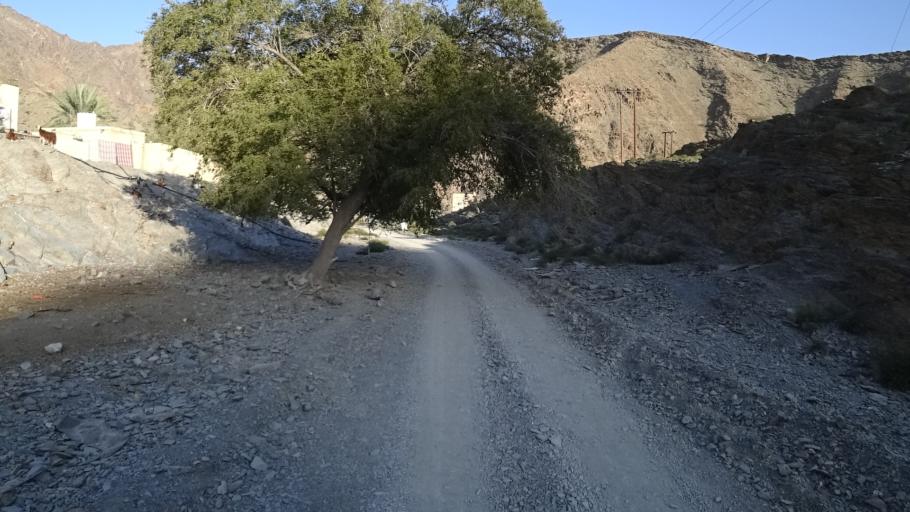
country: OM
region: Al Batinah
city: Rustaq
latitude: 23.2667
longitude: 57.3973
